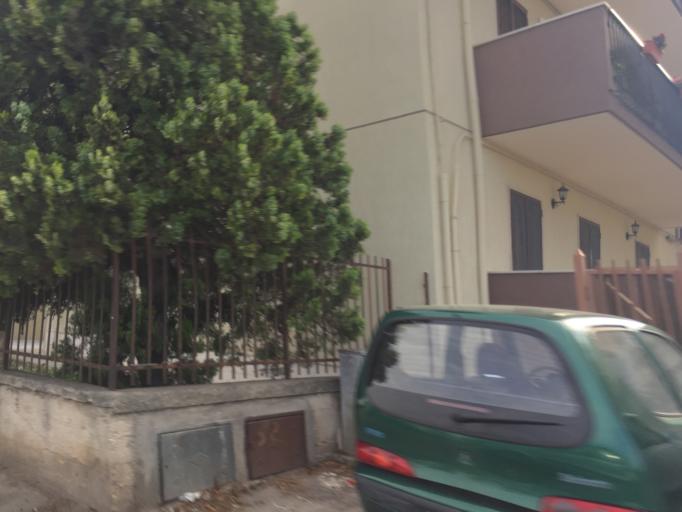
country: IT
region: Apulia
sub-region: Provincia di Bari
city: Capurso
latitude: 41.0516
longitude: 16.9217
